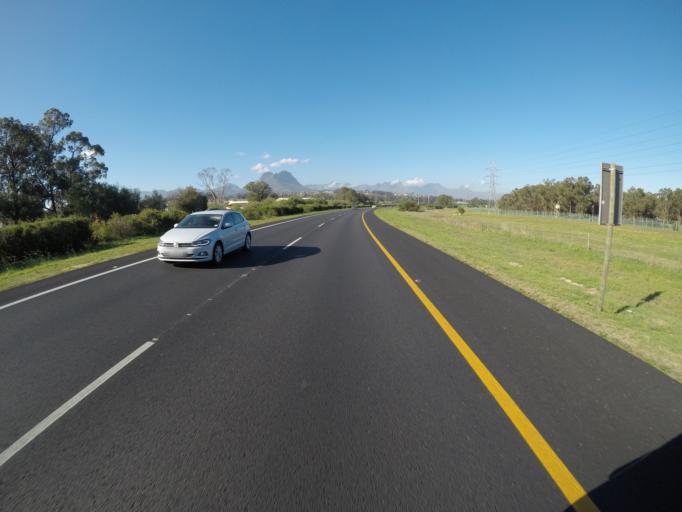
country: ZA
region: Western Cape
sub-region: Cape Winelands District Municipality
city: Stellenbosch
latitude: -34.0585
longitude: 18.7896
